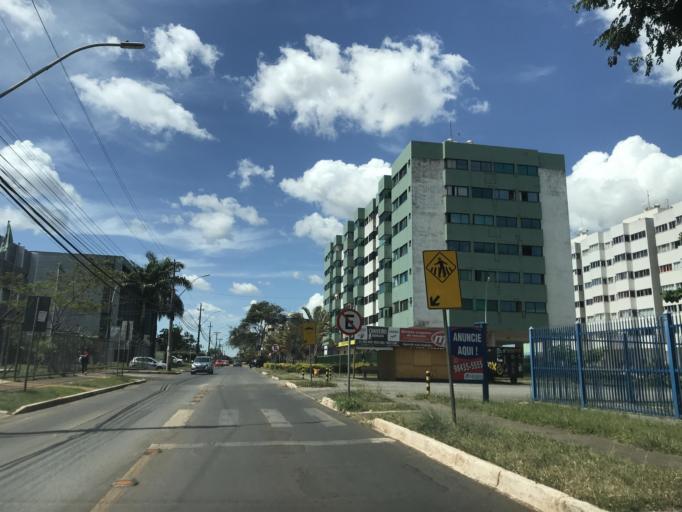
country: BR
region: Federal District
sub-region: Brasilia
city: Brasilia
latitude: -15.6513
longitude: -47.7933
